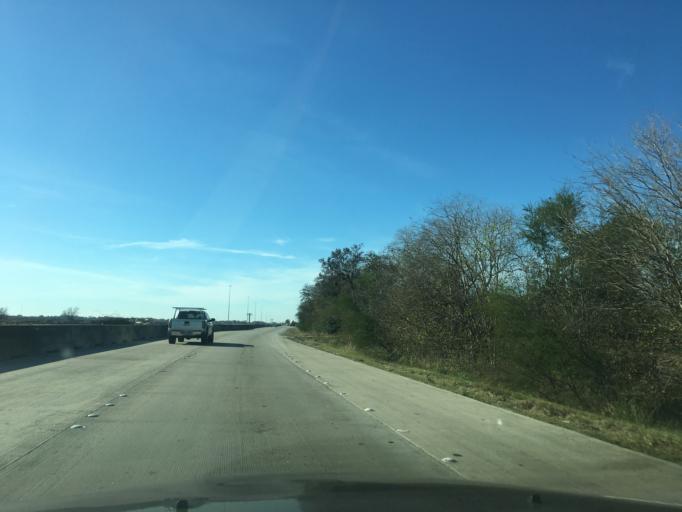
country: US
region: Texas
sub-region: Fort Bend County
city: Rosenberg
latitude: 29.5322
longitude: -95.8220
